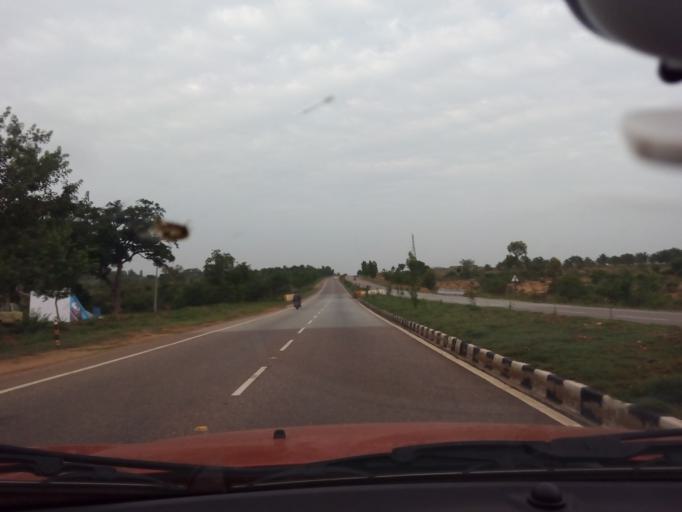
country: IN
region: Karnataka
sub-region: Mandya
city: Belluru
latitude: 12.9729
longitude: 76.8209
